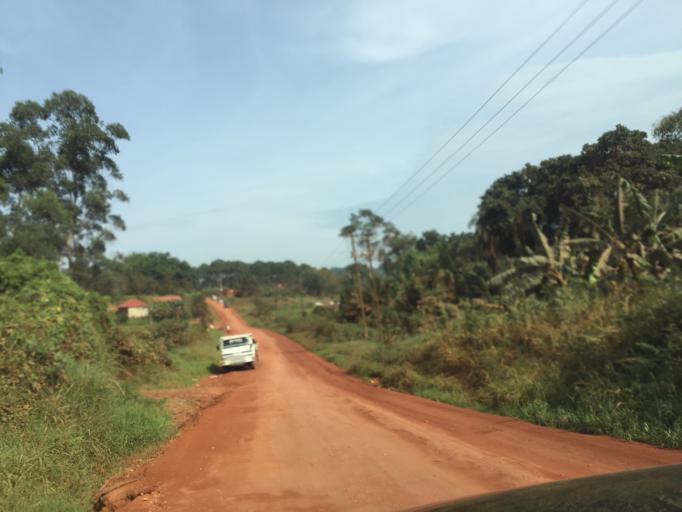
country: UG
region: Central Region
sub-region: Wakiso District
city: Wakiso
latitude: 0.4506
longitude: 32.5759
